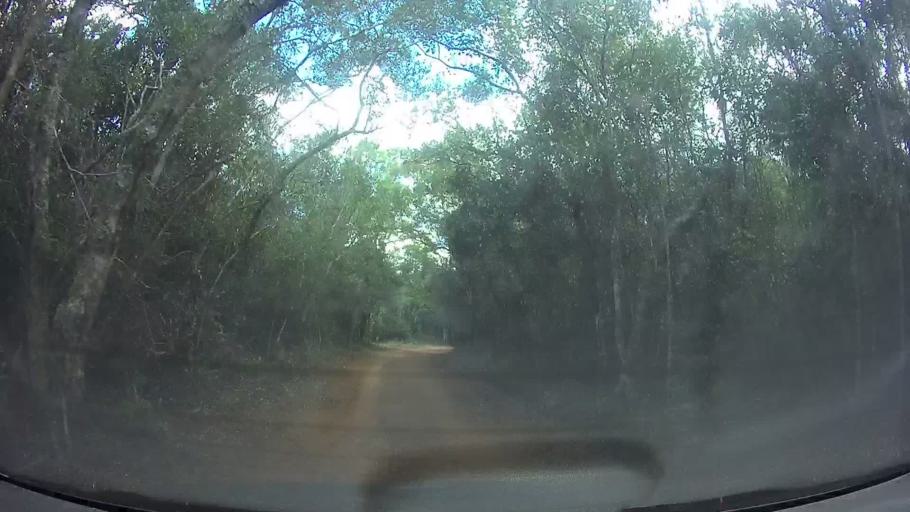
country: PY
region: Paraguari
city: La Colmena
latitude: -25.9745
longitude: -56.7279
